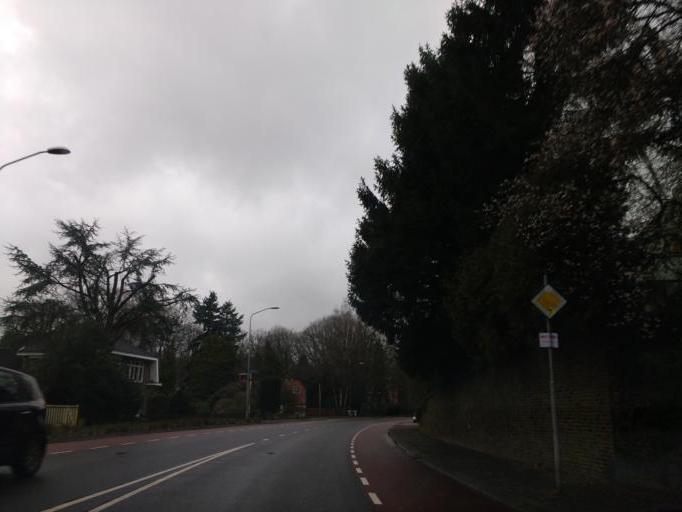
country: NL
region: Gelderland
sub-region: Gemeente Groesbeek
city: Berg en Dal
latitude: 51.8279
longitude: 5.9030
